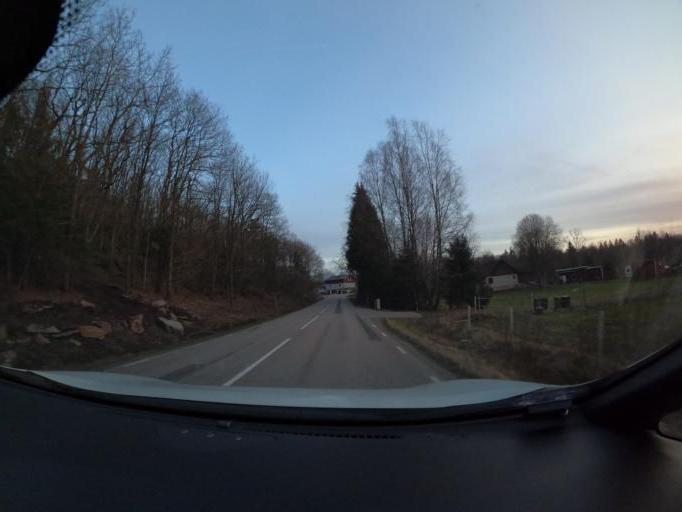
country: SE
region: Vaestra Goetaland
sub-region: Harryda Kommun
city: Landvetter
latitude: 57.6374
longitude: 12.1814
